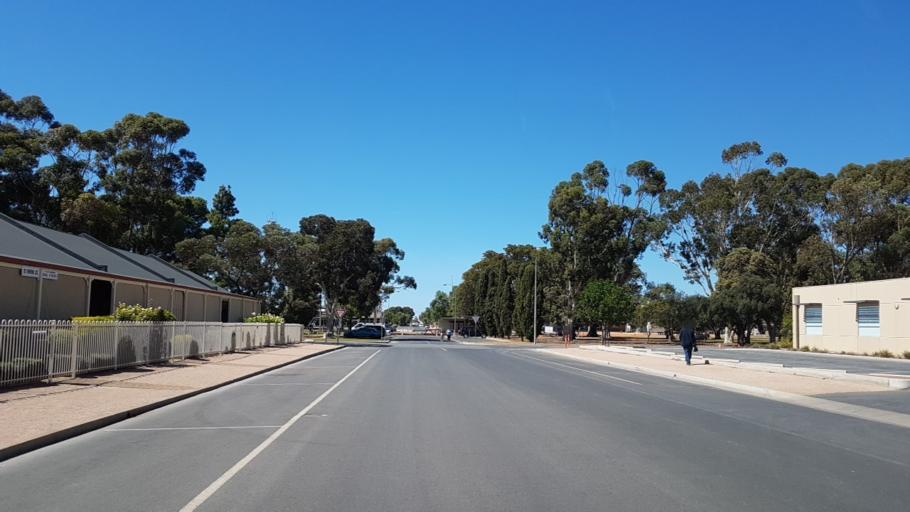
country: AU
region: South Australia
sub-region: Copper Coast
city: Kadina
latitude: -33.9612
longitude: 137.7155
